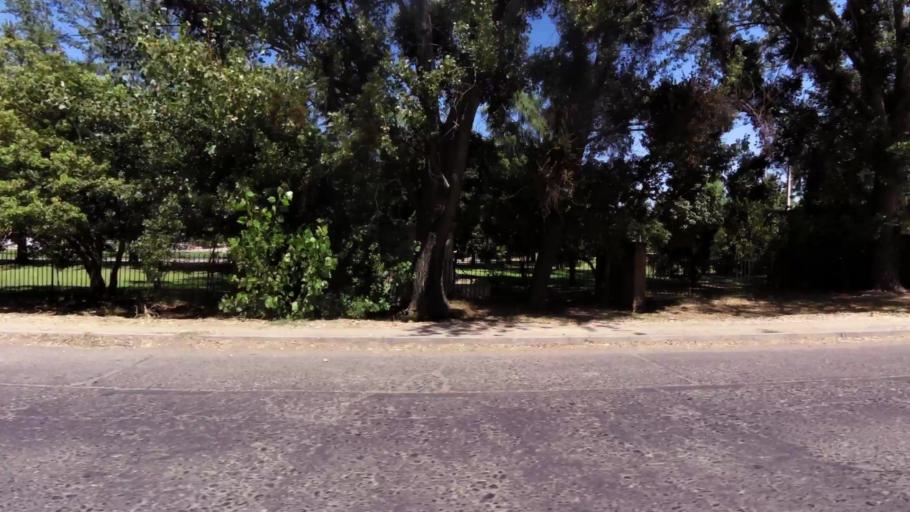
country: CL
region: Maule
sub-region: Provincia de Talca
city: Talca
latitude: -35.4016
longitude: -71.6348
